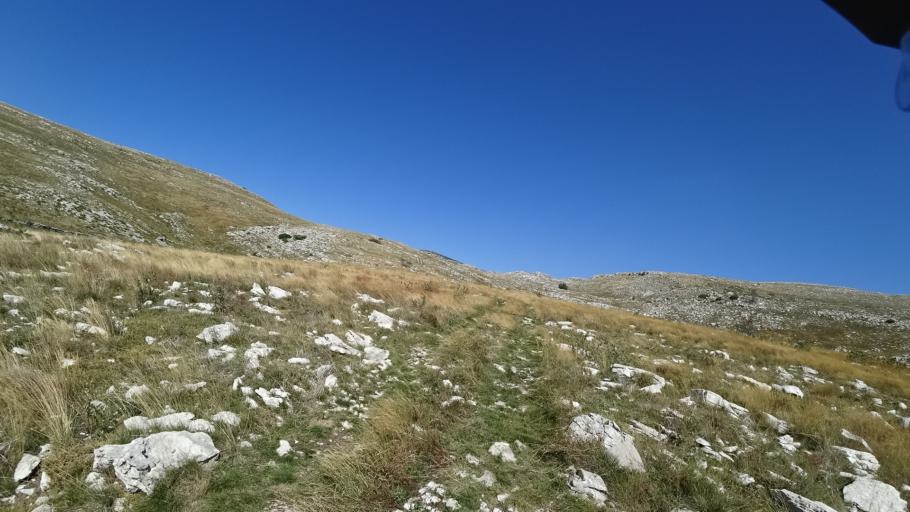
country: HR
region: Splitsko-Dalmatinska
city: Hrvace
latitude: 43.9216
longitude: 16.6063
